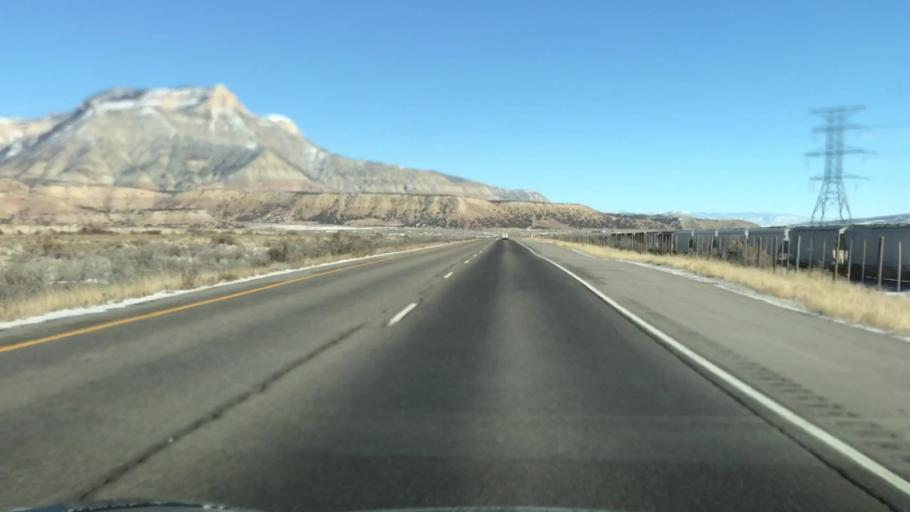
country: US
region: Colorado
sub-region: Garfield County
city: Battlement Mesa
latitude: 39.4694
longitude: -108.0287
